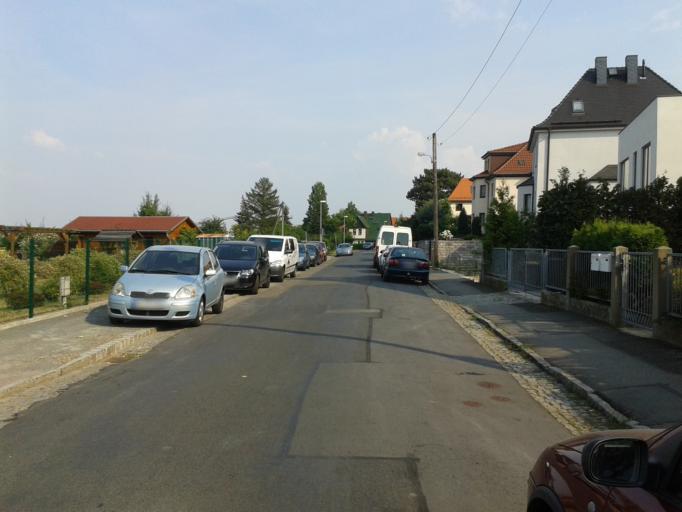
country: DE
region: Saxony
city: Bannewitz
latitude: 51.0309
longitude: 13.6948
